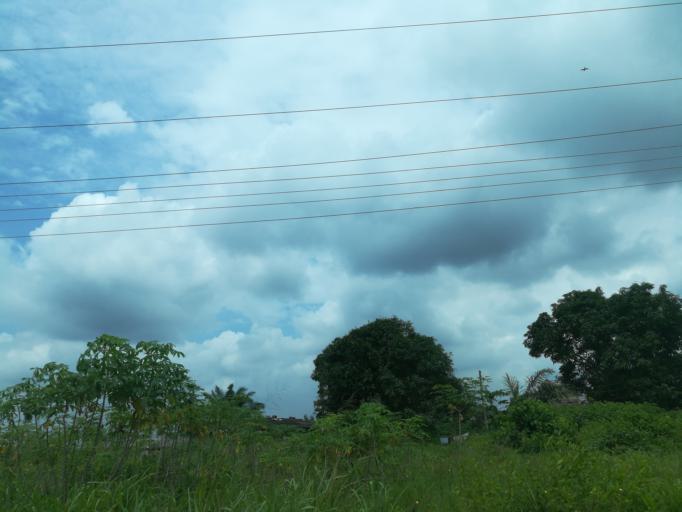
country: NG
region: Lagos
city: Ejirin
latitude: 6.6293
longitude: 3.7078
